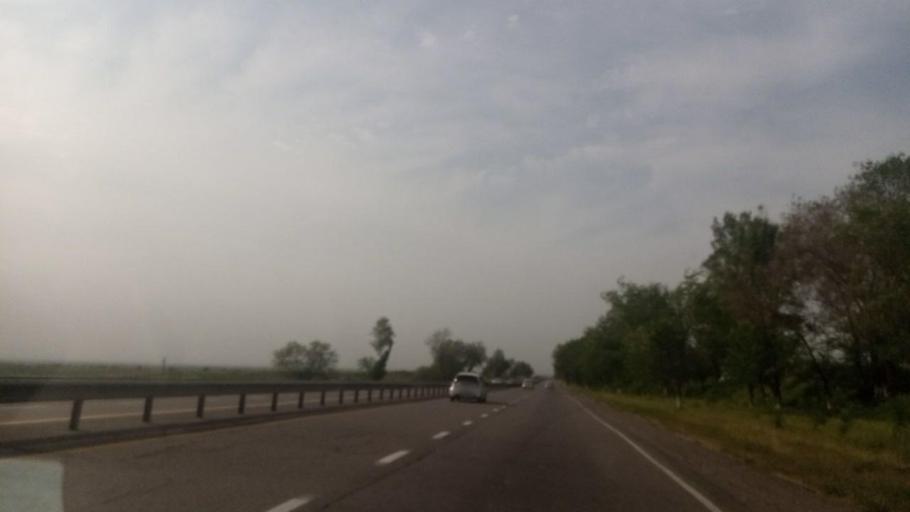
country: UZ
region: Toshkent
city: Tuytepa
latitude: 41.1026
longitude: 69.4546
